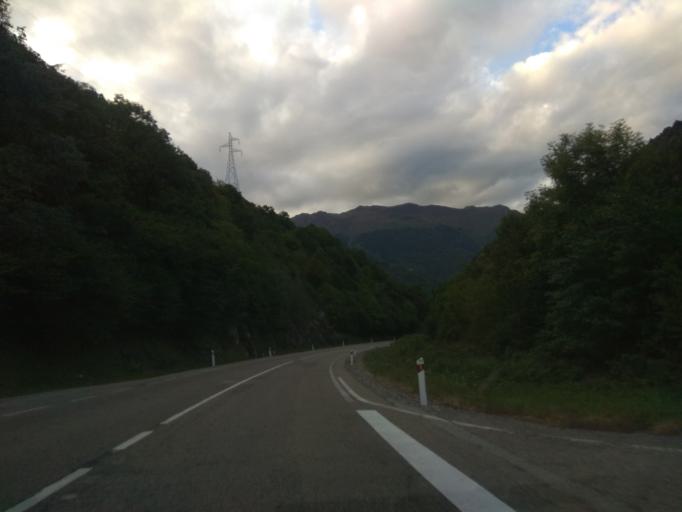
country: ES
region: Catalonia
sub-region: Provincia de Lleida
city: Les
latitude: 42.7591
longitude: 0.6929
